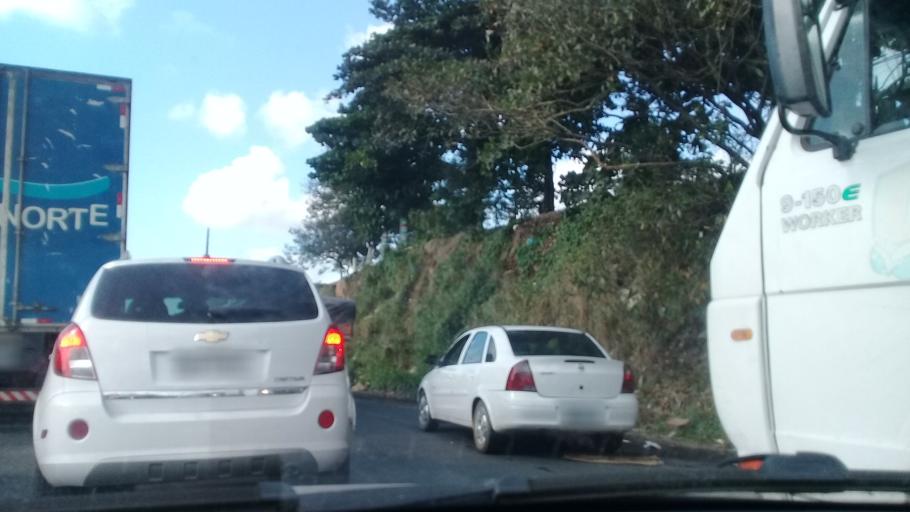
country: BR
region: Pernambuco
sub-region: Recife
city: Recife
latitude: -8.0782
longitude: -34.9432
